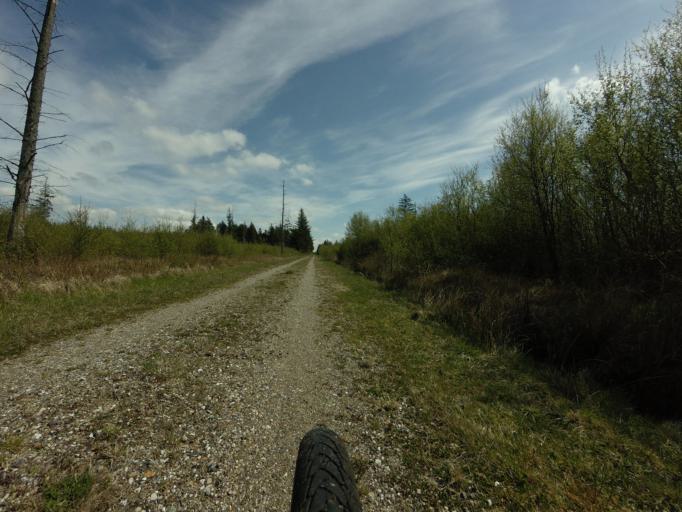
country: DK
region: North Denmark
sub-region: Jammerbugt Kommune
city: Brovst
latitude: 57.1691
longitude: 9.5451
